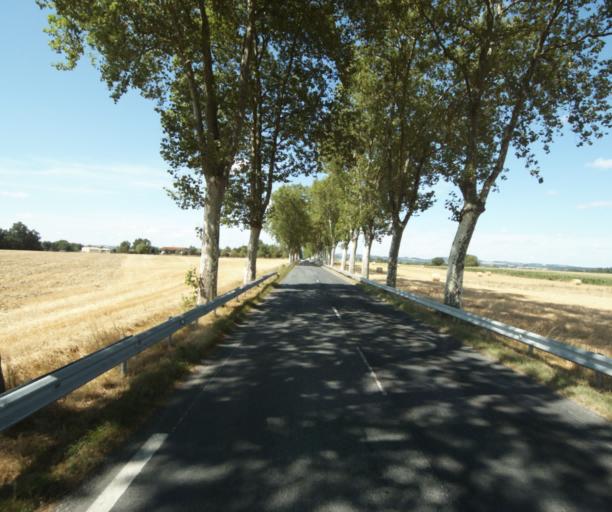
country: FR
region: Midi-Pyrenees
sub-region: Departement de la Haute-Garonne
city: Revel
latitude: 43.4925
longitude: 2.0130
